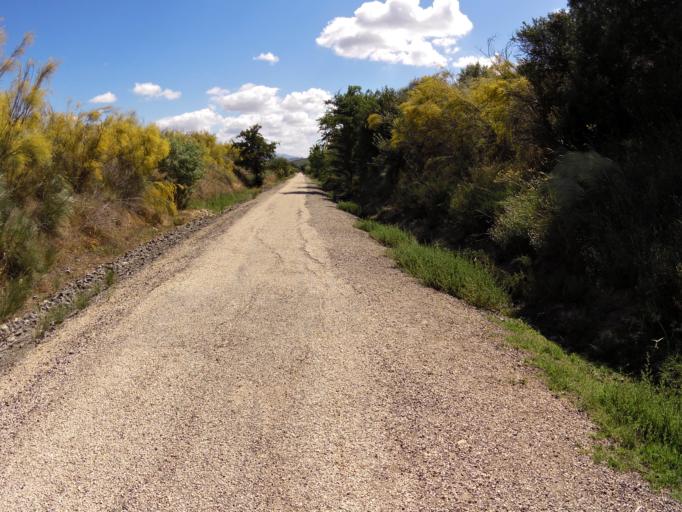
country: ES
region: Andalusia
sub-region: Provincia de Jaen
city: Alcaudete
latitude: 37.6196
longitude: -4.1053
